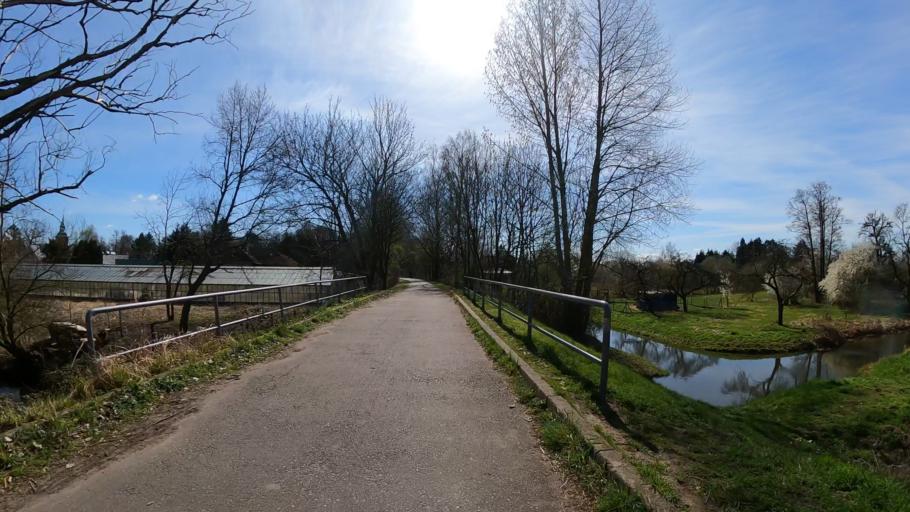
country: DE
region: Hamburg
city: Rothenburgsort
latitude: 53.4764
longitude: 10.0807
